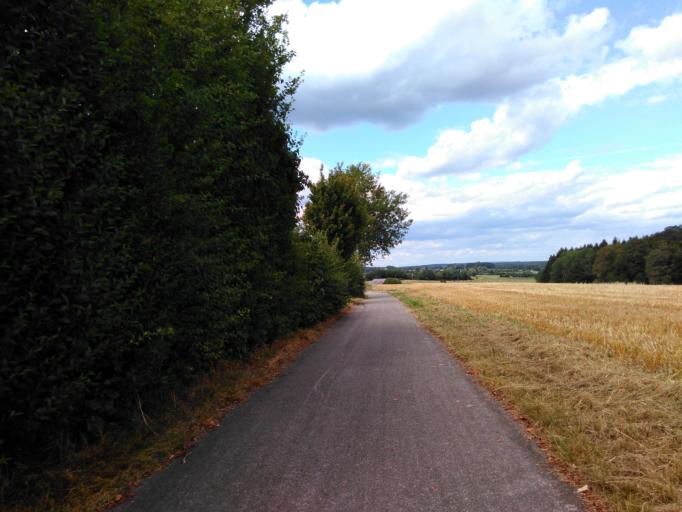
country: LU
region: Grevenmacher
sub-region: Canton d'Echternach
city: Consdorf
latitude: 49.7675
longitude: 6.3428
